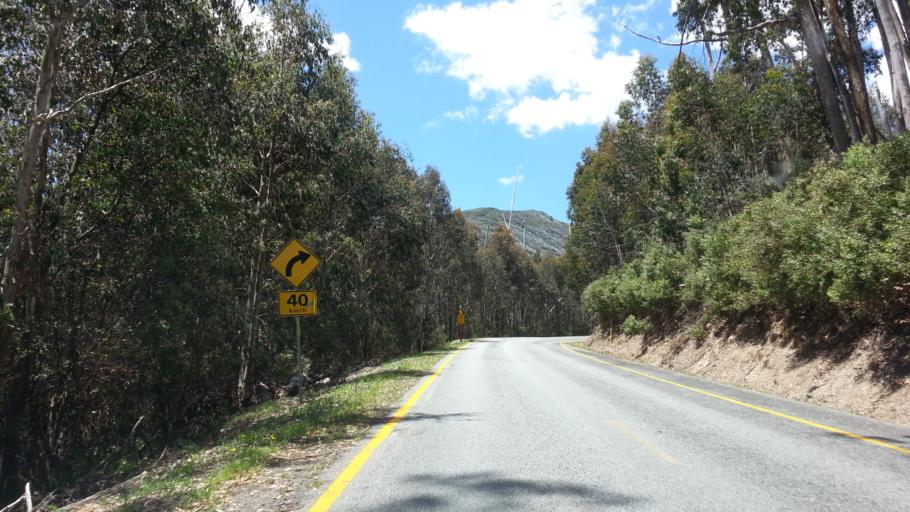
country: AU
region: Victoria
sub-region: Alpine
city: Mount Beauty
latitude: -36.8445
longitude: 147.2635
